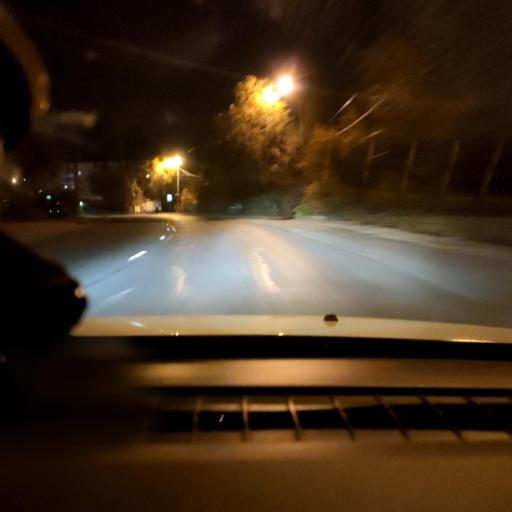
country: RU
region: Samara
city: Rozhdestveno
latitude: 53.1458
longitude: 50.0520
